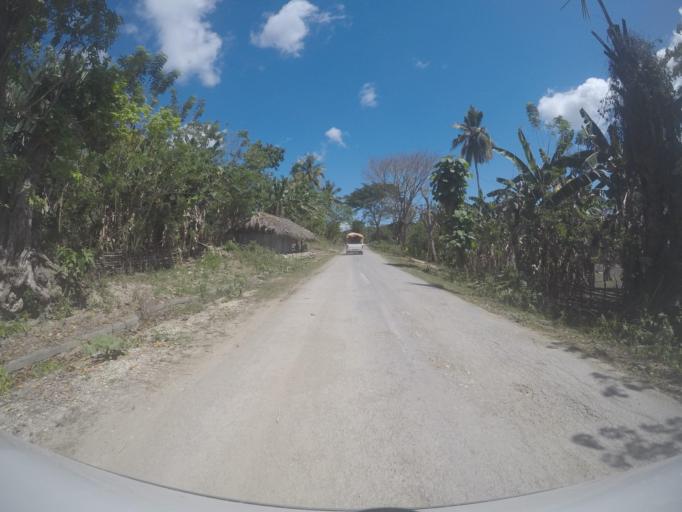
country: TL
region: Viqueque
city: Viqueque
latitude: -8.9171
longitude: 126.3974
